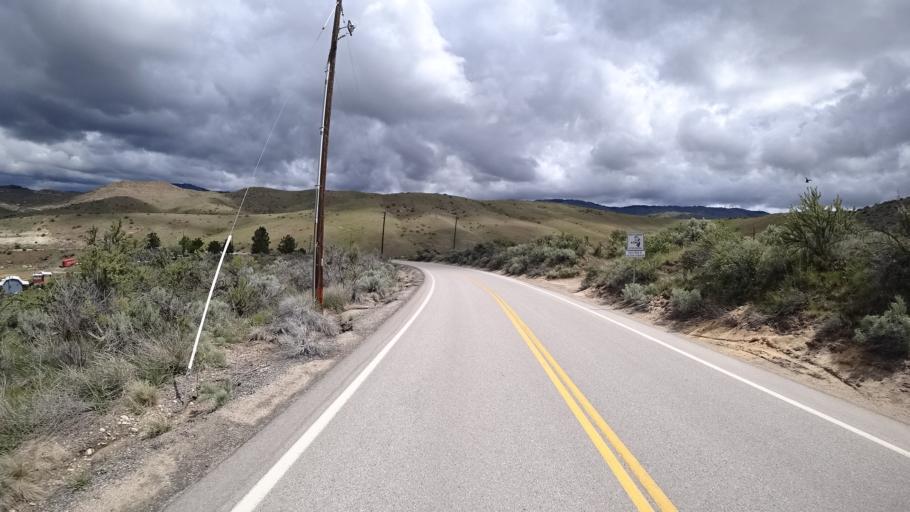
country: US
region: Idaho
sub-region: Ada County
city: Boise
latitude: 43.6721
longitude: -116.1817
